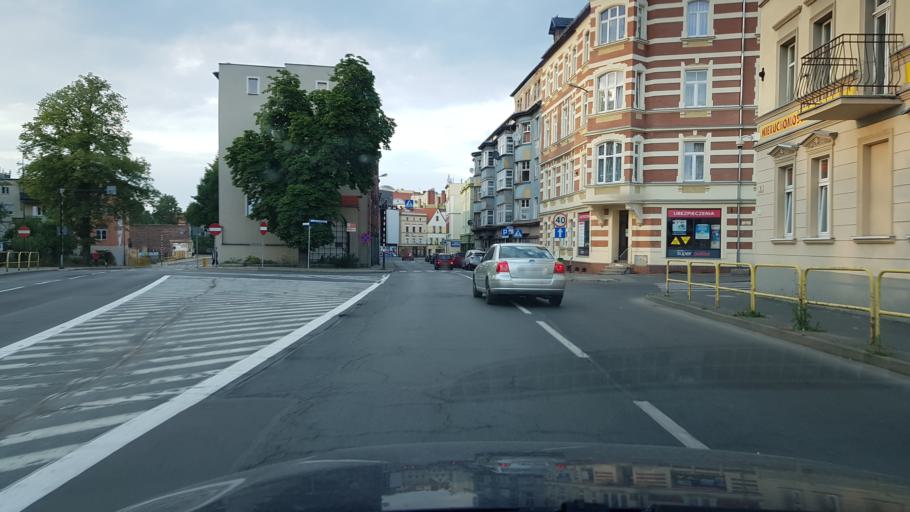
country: PL
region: Lower Silesian Voivodeship
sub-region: Jelenia Gora
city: Jelenia Gora
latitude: 50.8993
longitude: 15.7325
